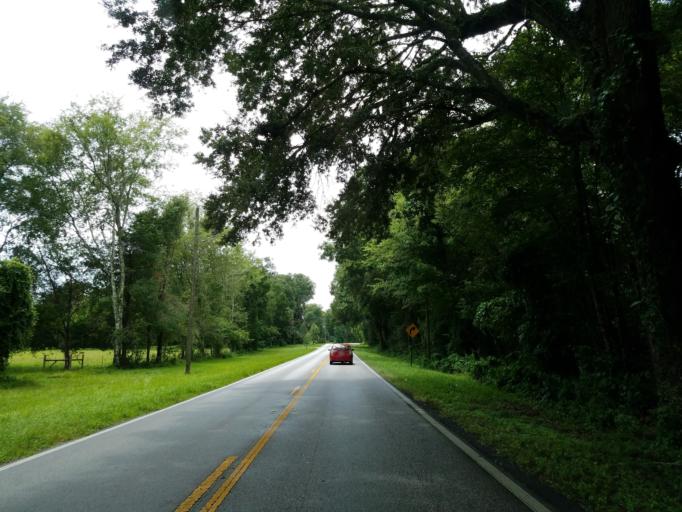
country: US
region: Florida
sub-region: Sumter County
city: Bushnell
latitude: 28.6910
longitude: -82.2057
